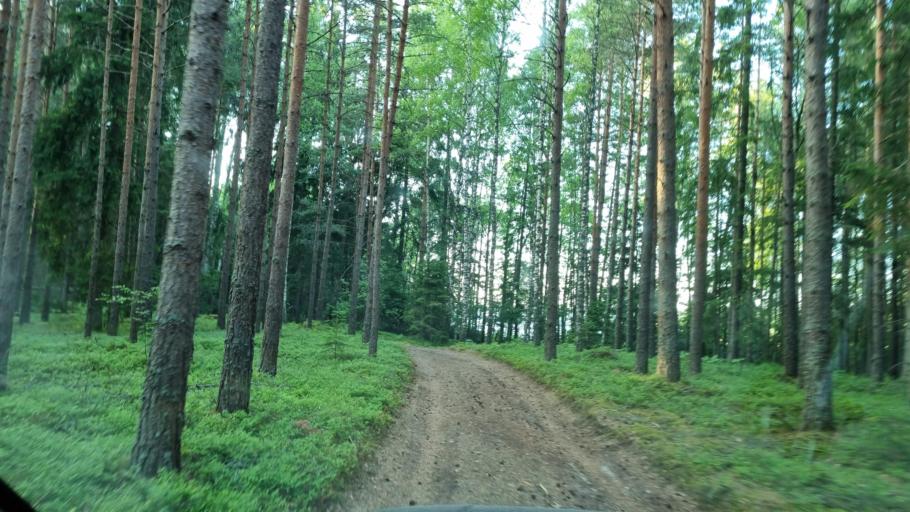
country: LV
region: Kuldigas Rajons
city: Kuldiga
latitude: 57.1956
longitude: 22.1867
